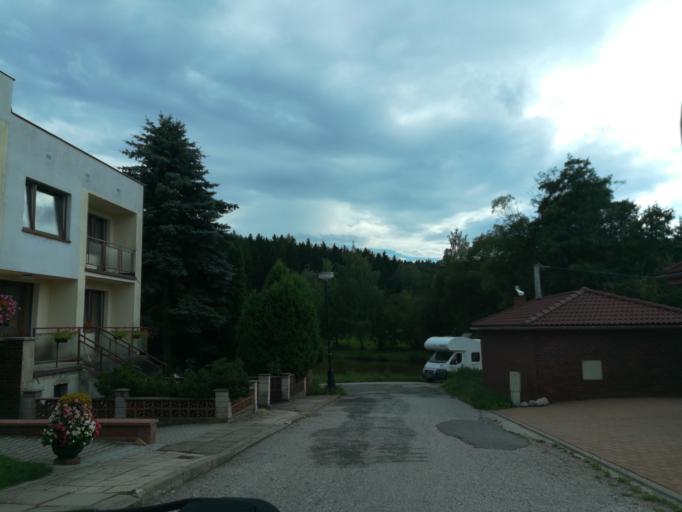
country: CZ
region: Kralovehradecky
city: Stara Paka
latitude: 50.4953
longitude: 15.4991
